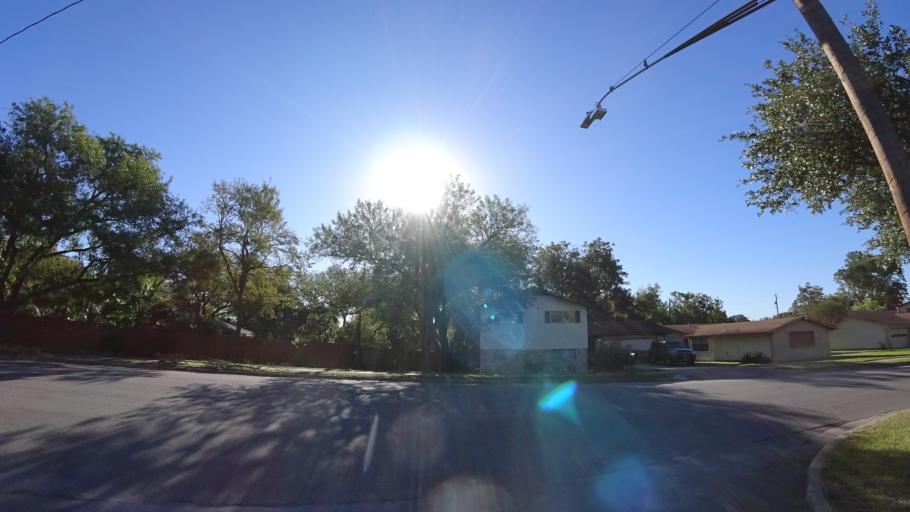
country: US
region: Texas
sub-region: Travis County
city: Austin
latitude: 30.3067
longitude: -97.6764
